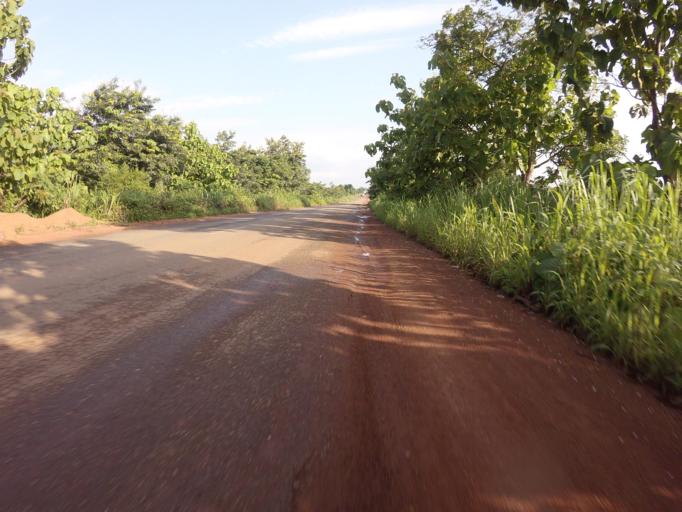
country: GH
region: Volta
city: Hohoe
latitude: 7.0367
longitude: 0.4270
